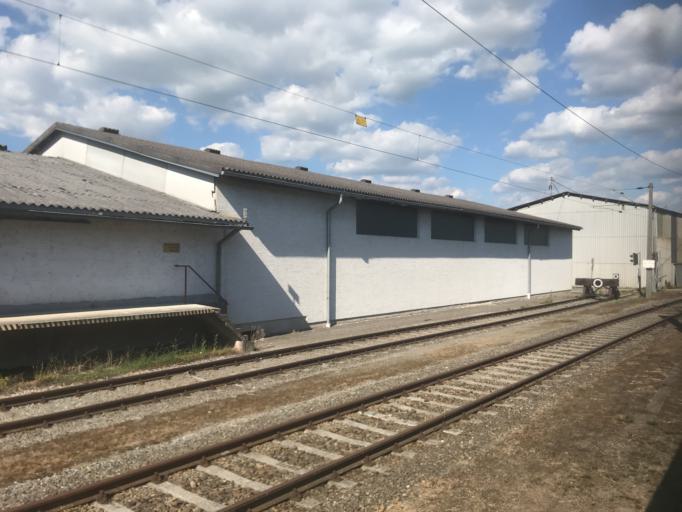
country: AT
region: Upper Austria
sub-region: Politischer Bezirk Freistadt
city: Freistadt
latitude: 48.4952
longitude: 14.4863
